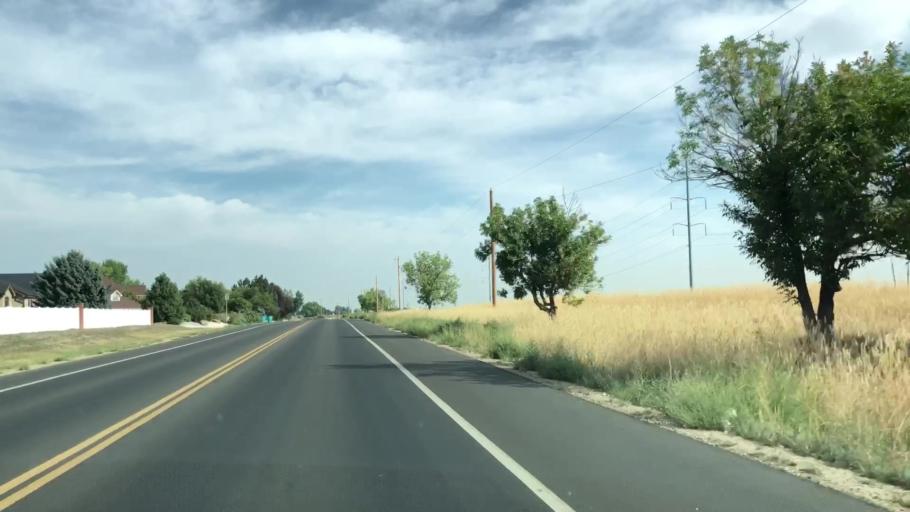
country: US
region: Colorado
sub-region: Larimer County
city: Loveland
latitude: 40.4343
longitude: -105.0454
